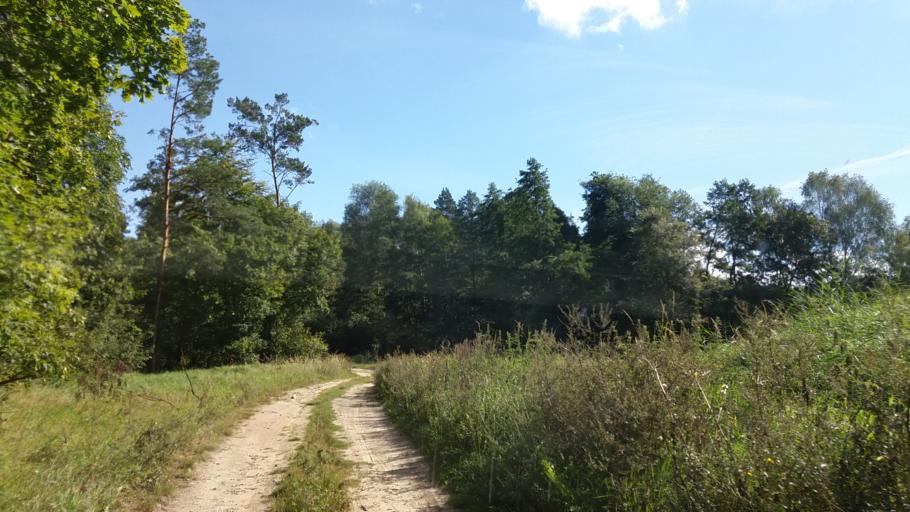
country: PL
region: West Pomeranian Voivodeship
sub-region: Powiat choszczenski
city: Krzecin
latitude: 53.1412
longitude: 15.4809
